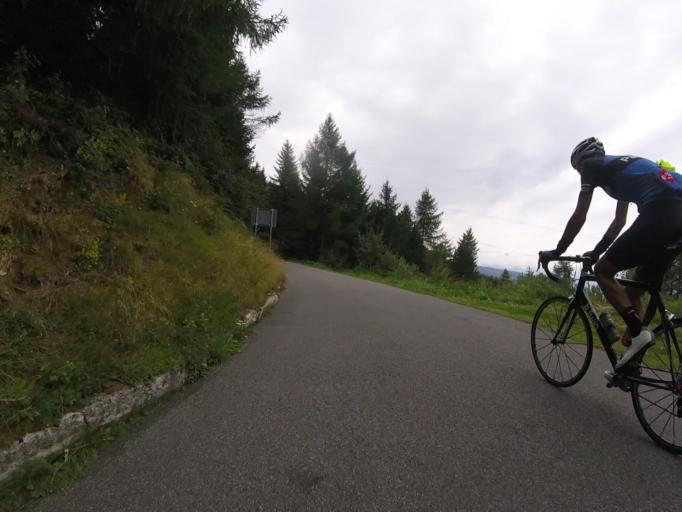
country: IT
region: Lombardy
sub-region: Provincia di Sondrio
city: Mazzo di Valtellina
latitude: 46.2585
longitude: 10.2916
